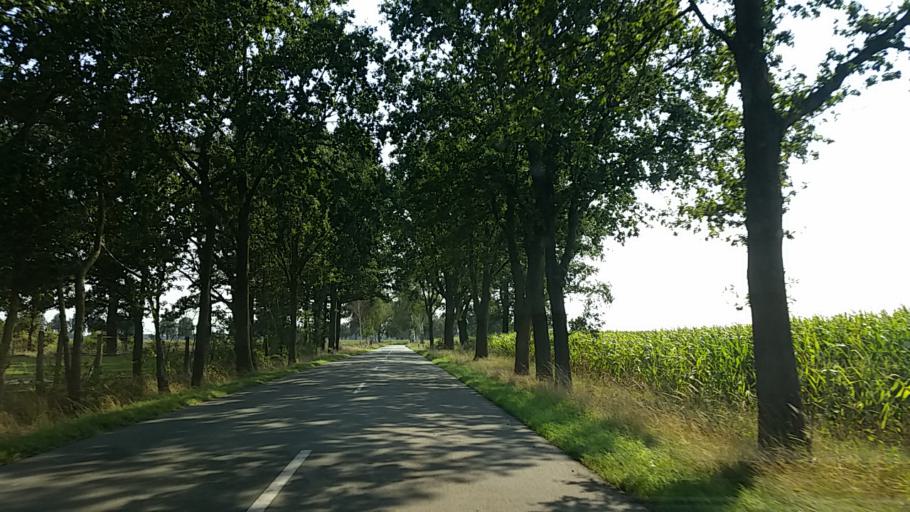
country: DE
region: Mecklenburg-Vorpommern
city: Domitz
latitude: 53.1233
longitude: 11.2402
